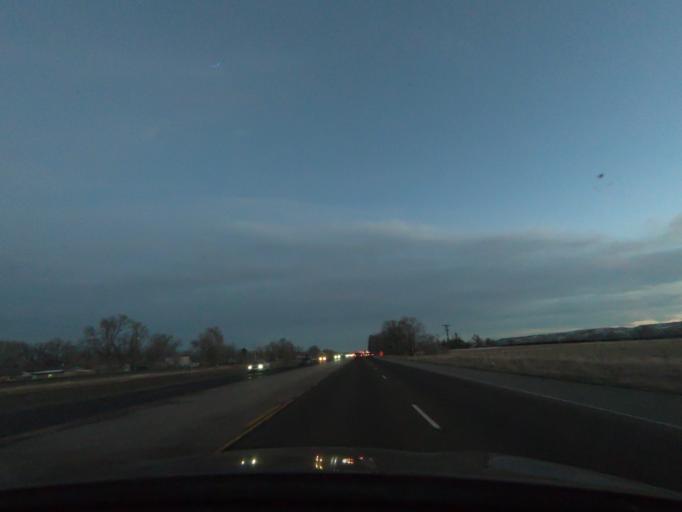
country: US
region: Colorado
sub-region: El Paso County
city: Stratmoor
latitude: 38.7590
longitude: -104.7518
